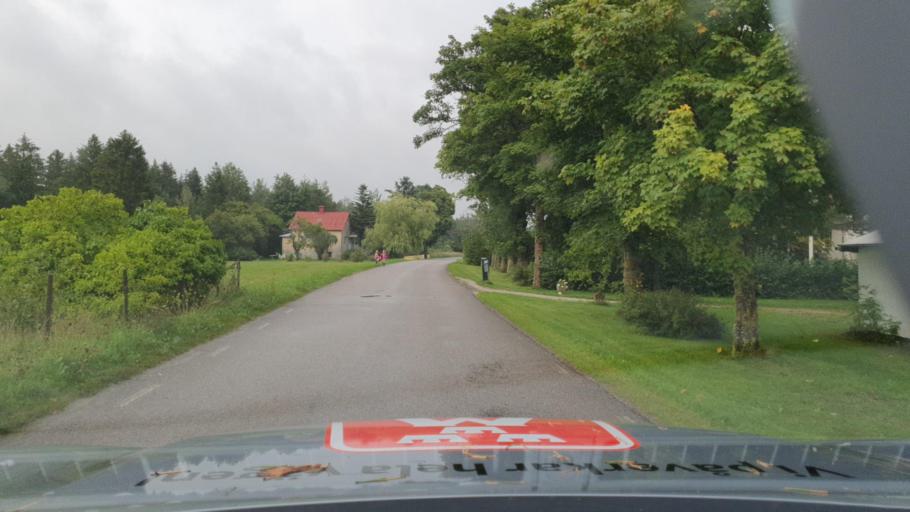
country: SE
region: Gotland
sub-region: Gotland
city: Visby
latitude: 57.6552
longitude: 18.5337
